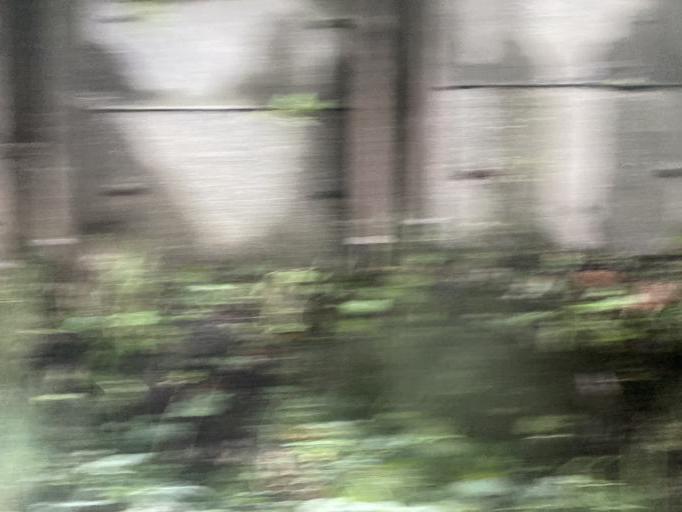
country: US
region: Washington
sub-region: King County
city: Seattle
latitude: 47.6414
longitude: -122.4146
